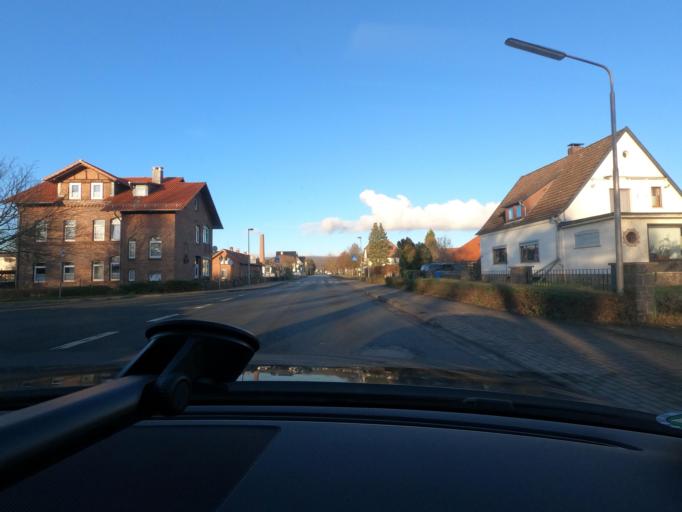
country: DE
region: Lower Saxony
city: Herzberg am Harz
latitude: 51.6450
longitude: 10.3307
